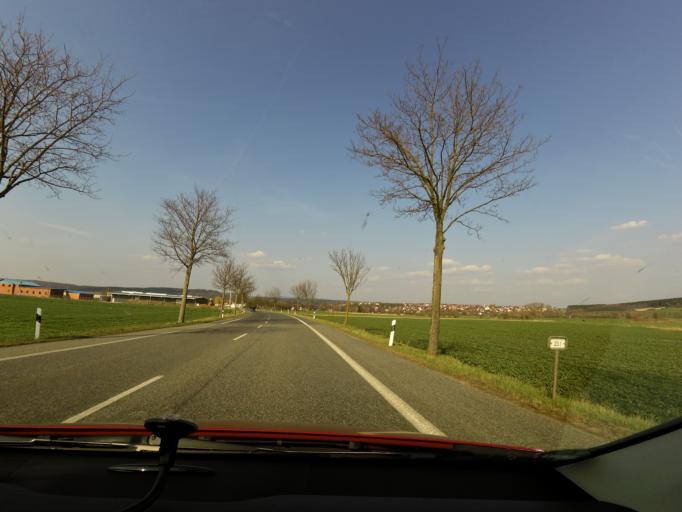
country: DE
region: Lower Saxony
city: Gieboldehausen
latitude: 51.5979
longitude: 10.2014
